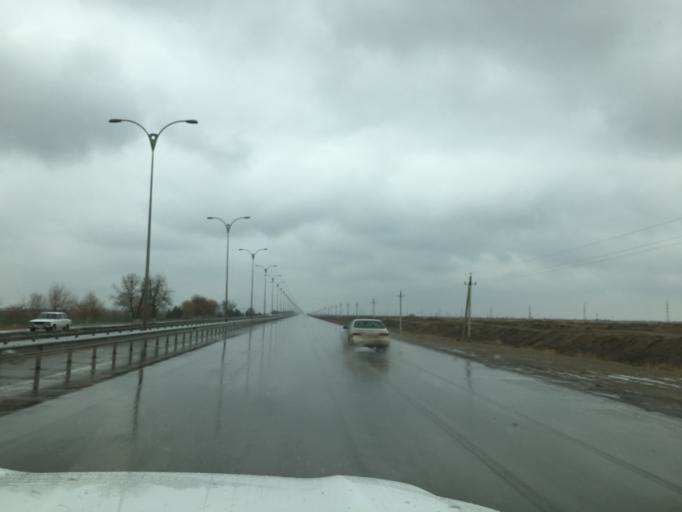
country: TM
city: Murgab
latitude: 37.5096
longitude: 61.9398
